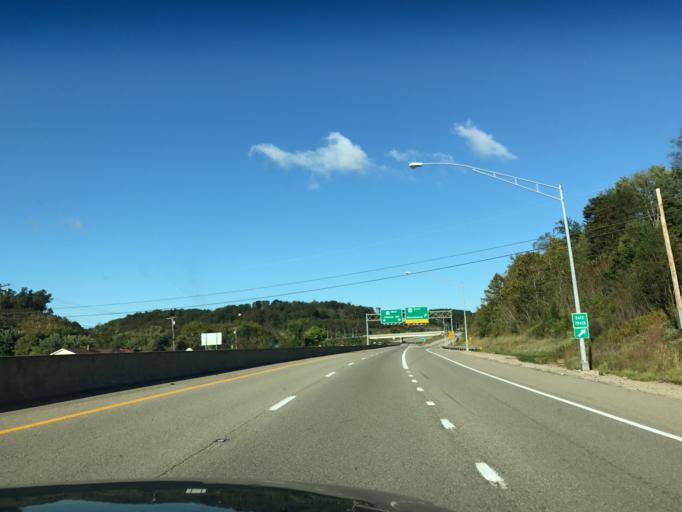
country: US
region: West Virginia
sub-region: Wood County
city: Blennerhassett
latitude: 39.2513
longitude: -81.6048
